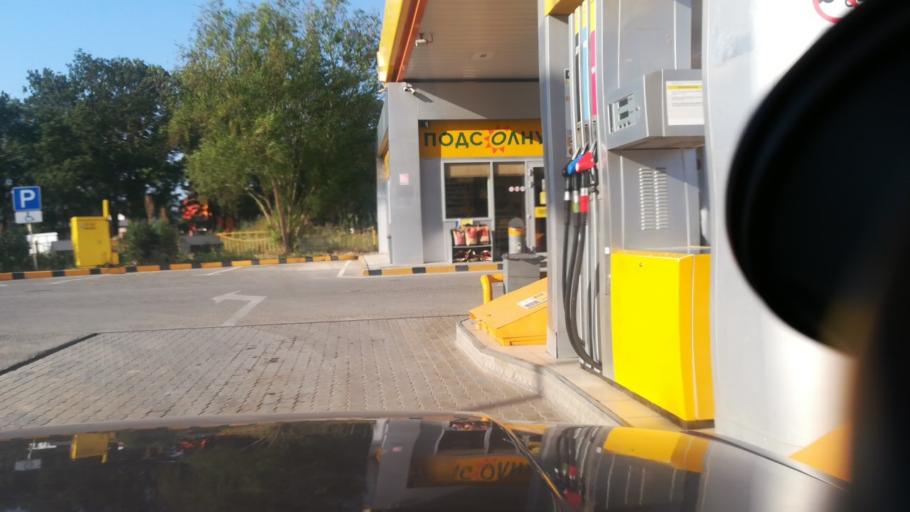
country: RU
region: Krasnodarskiy
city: Vityazevo
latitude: 45.0012
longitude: 37.2926
